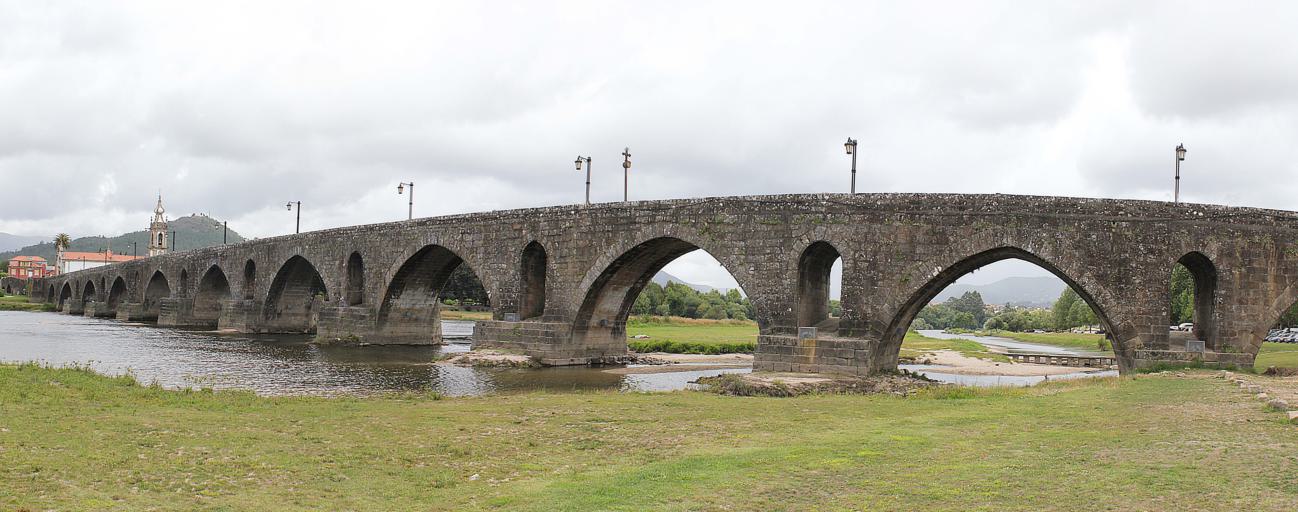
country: PT
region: Viana do Castelo
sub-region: Ponte de Lima
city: Ponte de Lima
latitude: 41.7683
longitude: -8.5856
